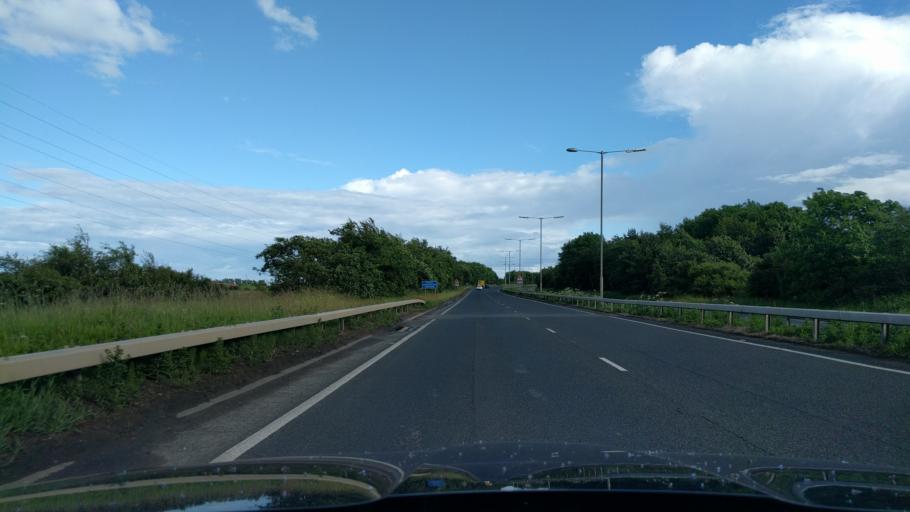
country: GB
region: England
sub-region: Northumberland
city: Newbiggin-by-the-Sea
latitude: 55.1818
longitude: -1.5349
